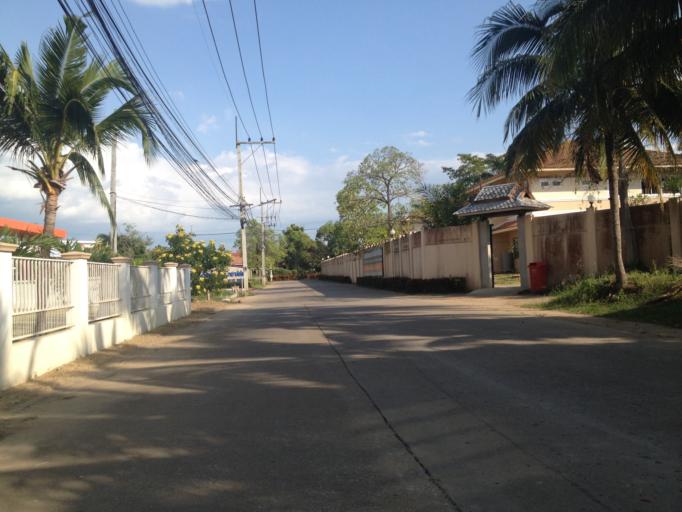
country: TH
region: Chiang Mai
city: Hang Dong
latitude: 18.6974
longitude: 98.9428
